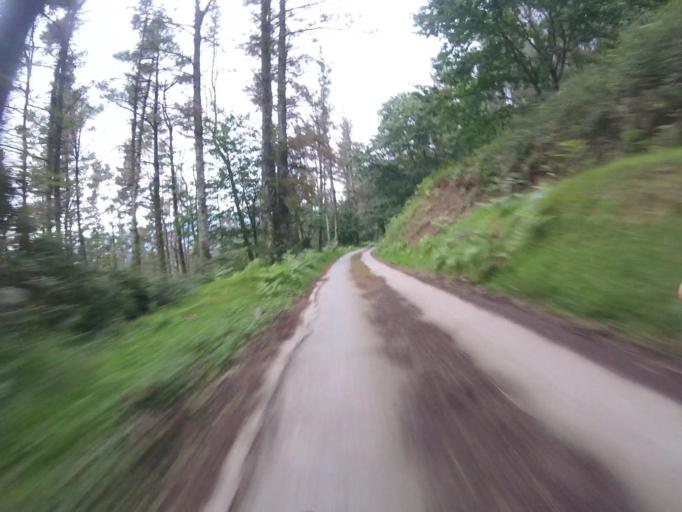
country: ES
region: Basque Country
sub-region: Provincia de Guipuzcoa
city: Errenteria
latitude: 43.2670
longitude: -1.8340
